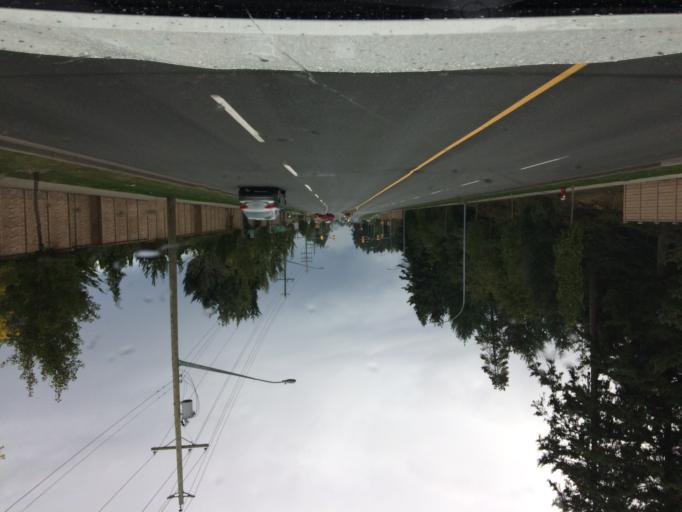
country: CA
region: British Columbia
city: Courtenay
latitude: 49.7074
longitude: -124.9618
